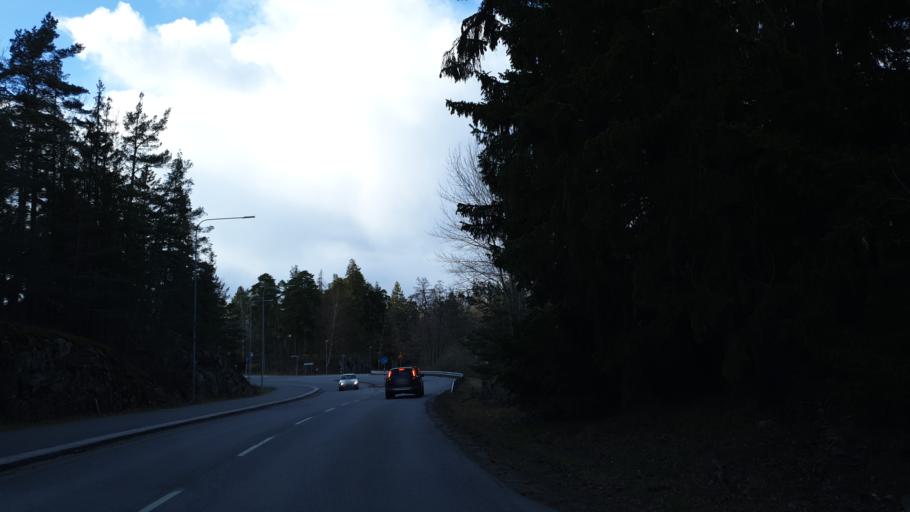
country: SE
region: Stockholm
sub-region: Lidingo
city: Lidingoe
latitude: 59.3826
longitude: 18.1196
